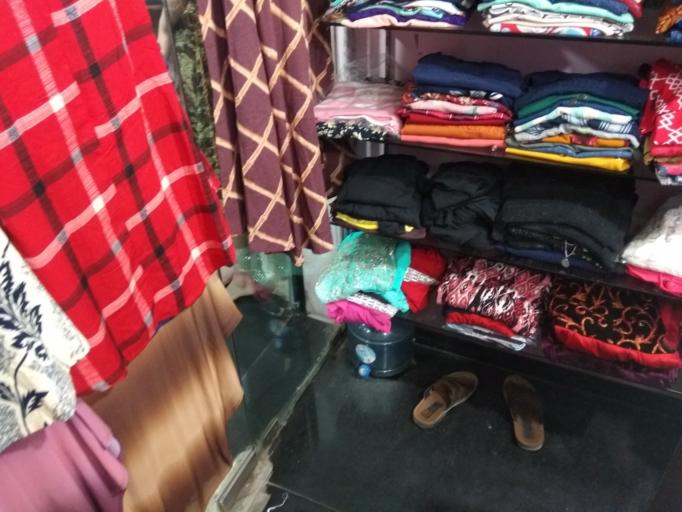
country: IN
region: Gujarat
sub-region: Ahmadabad
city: Sarkhej
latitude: 23.0132
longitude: 72.5201
